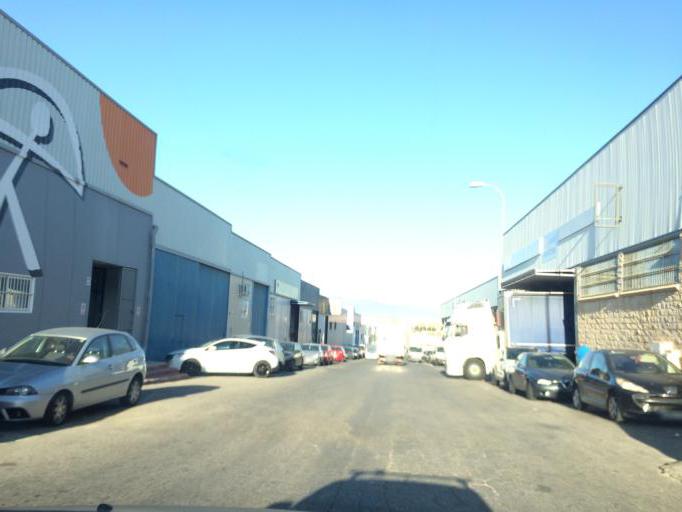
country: ES
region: Andalusia
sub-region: Provincia de Almeria
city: Viator
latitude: 36.8816
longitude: -2.4165
